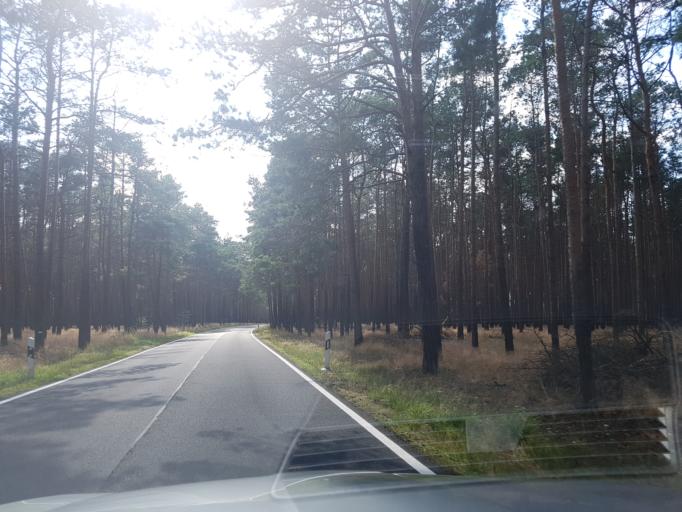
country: DE
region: Brandenburg
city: Schlieben
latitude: 51.6790
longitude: 13.3336
